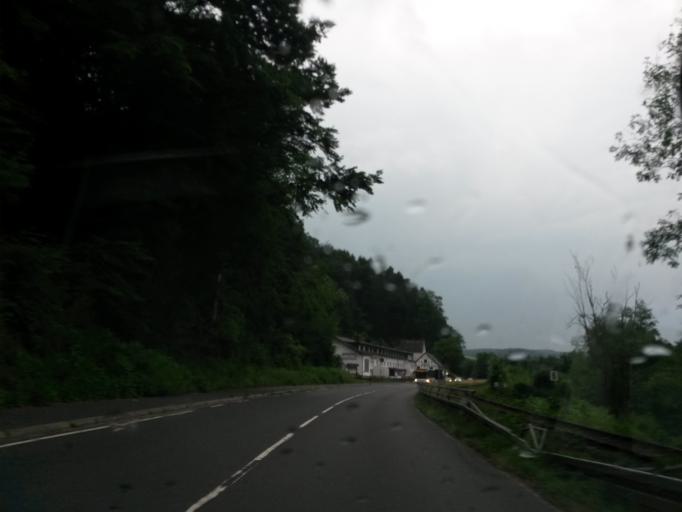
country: DE
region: North Rhine-Westphalia
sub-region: Regierungsbezirk Koln
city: Overath
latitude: 50.9498
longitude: 7.3092
